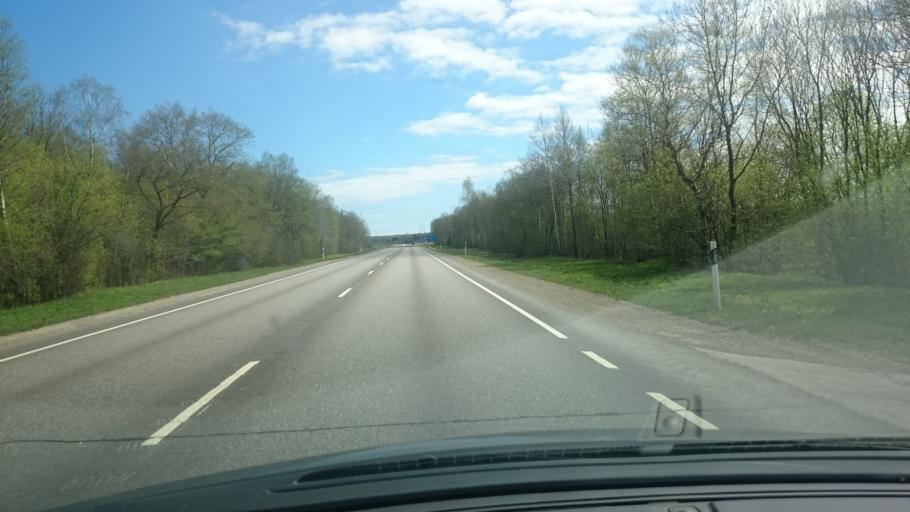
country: EE
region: Ida-Virumaa
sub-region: Kohtla-Jaerve linn
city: Kohtla-Jarve
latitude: 59.4207
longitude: 27.2637
